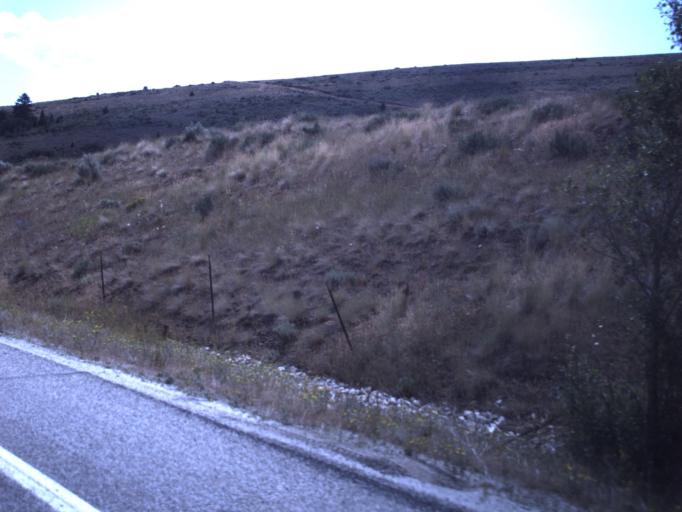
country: US
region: Idaho
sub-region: Bear Lake County
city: Paris
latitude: 41.9307
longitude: -111.4207
